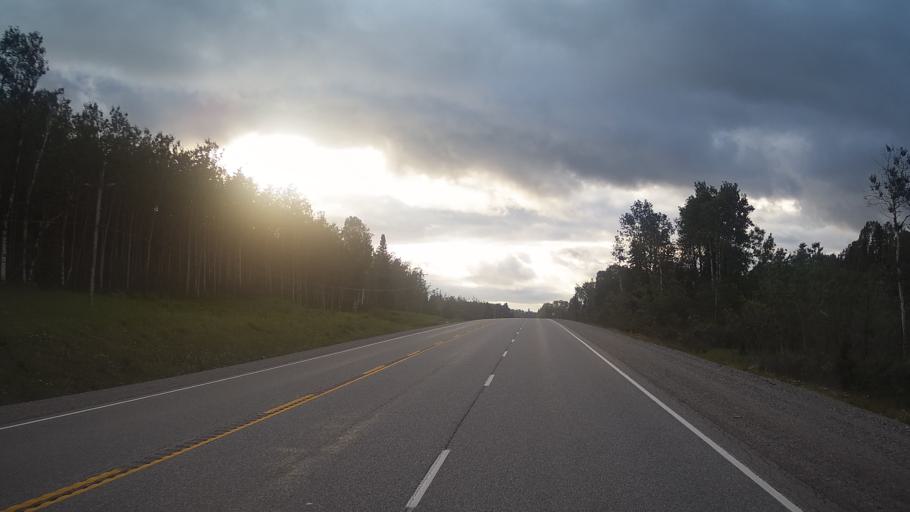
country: CA
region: Ontario
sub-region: Rainy River District
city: Atikokan
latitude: 49.0068
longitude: -90.4144
